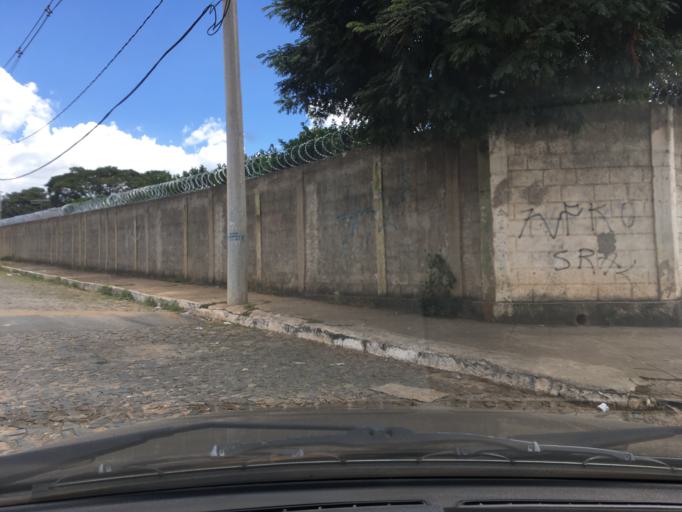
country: BR
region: Minas Gerais
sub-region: Mateus Leme
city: Mateus Leme
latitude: -19.9944
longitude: -44.4332
